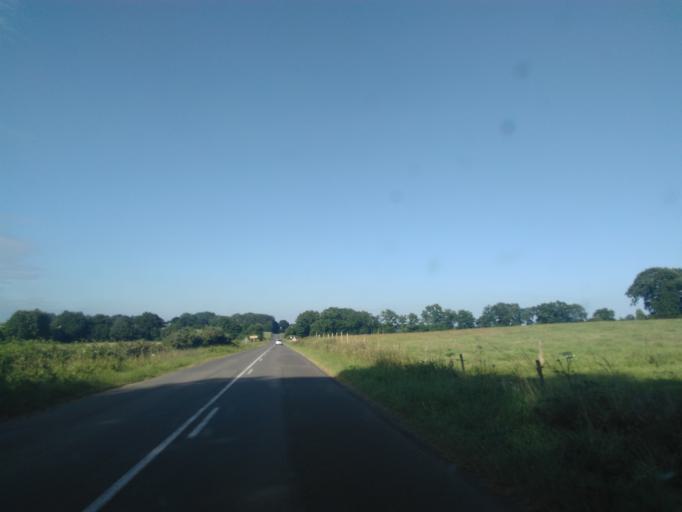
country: FR
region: Brittany
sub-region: Departement d'Ille-et-Vilaine
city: Geveze
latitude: 48.2164
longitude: -1.8261
